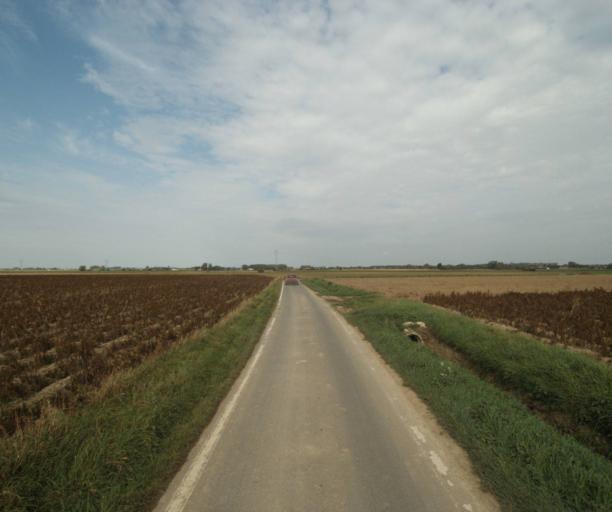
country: FR
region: Nord-Pas-de-Calais
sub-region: Departement du Nord
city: Salome
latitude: 50.5361
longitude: 2.8627
